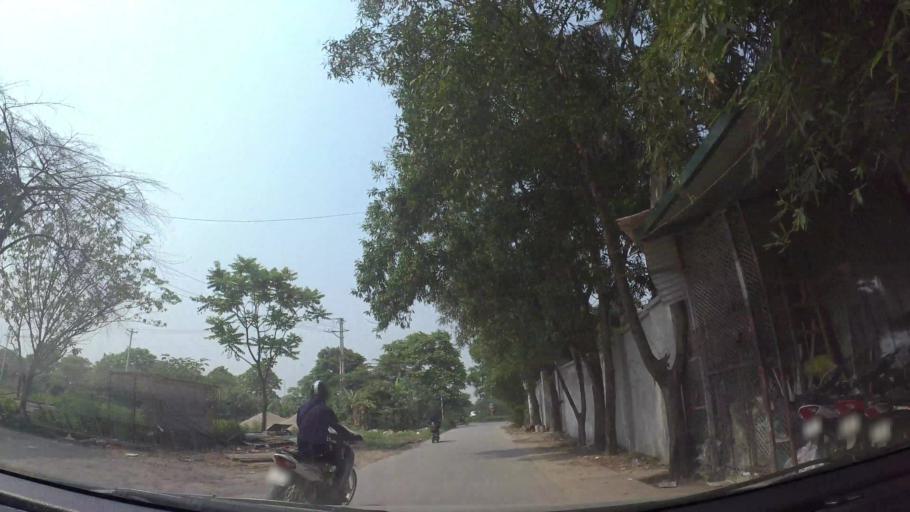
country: VN
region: Ha Noi
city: Cau Dien
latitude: 21.0056
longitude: 105.7591
